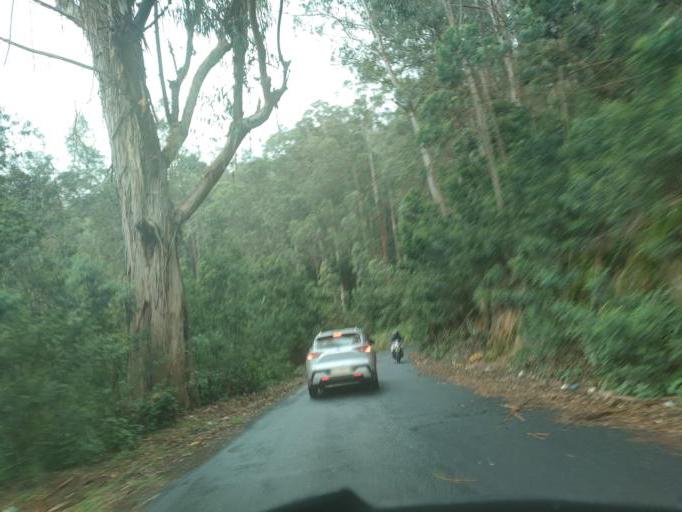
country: IN
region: Tamil Nadu
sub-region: Dindigul
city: Kodaikanal
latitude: 10.2418
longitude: 77.3557
